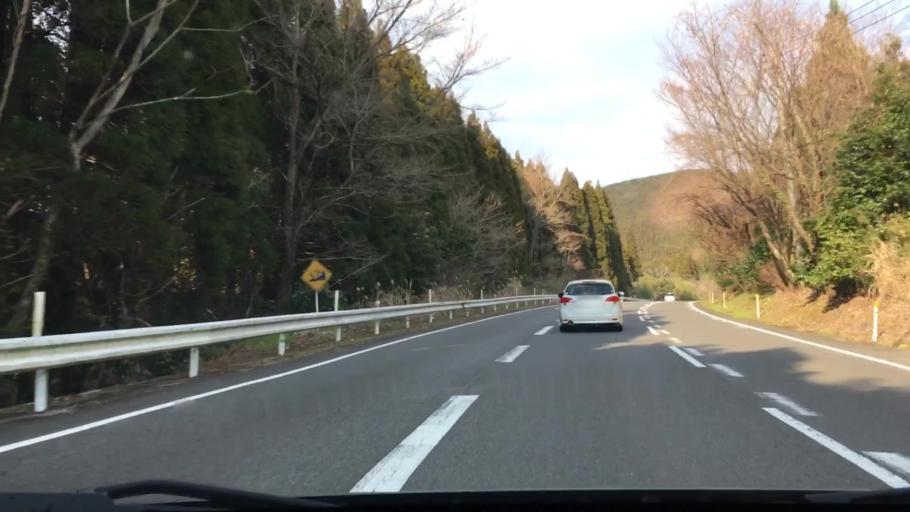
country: JP
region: Miyazaki
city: Miyazaki-shi
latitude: 31.7716
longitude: 131.3293
